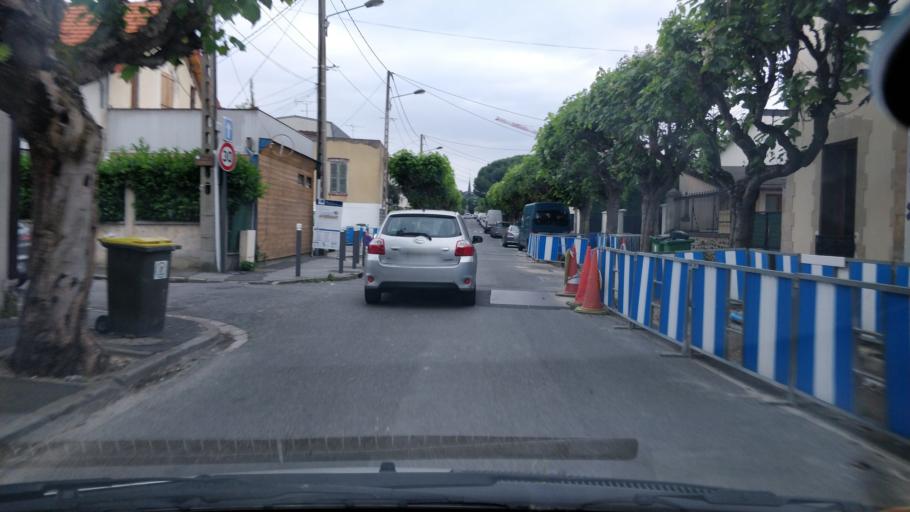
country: FR
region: Ile-de-France
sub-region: Departement de Seine-Saint-Denis
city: Le Raincy
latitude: 48.9051
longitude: 2.5247
